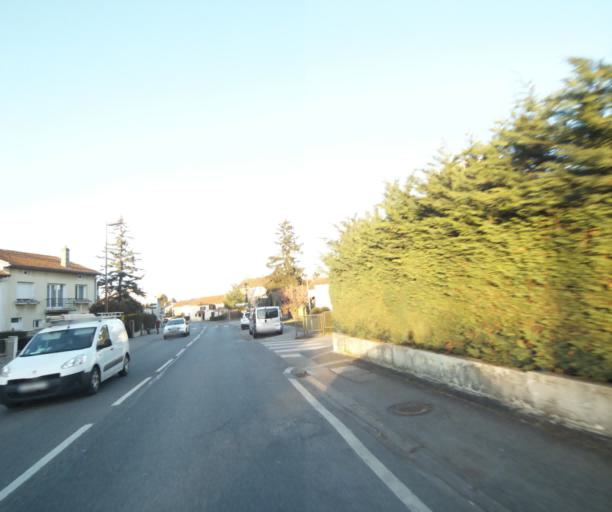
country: FR
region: Lorraine
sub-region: Departement de Meurthe-et-Moselle
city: Pulnoy
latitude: 48.7000
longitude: 6.2559
